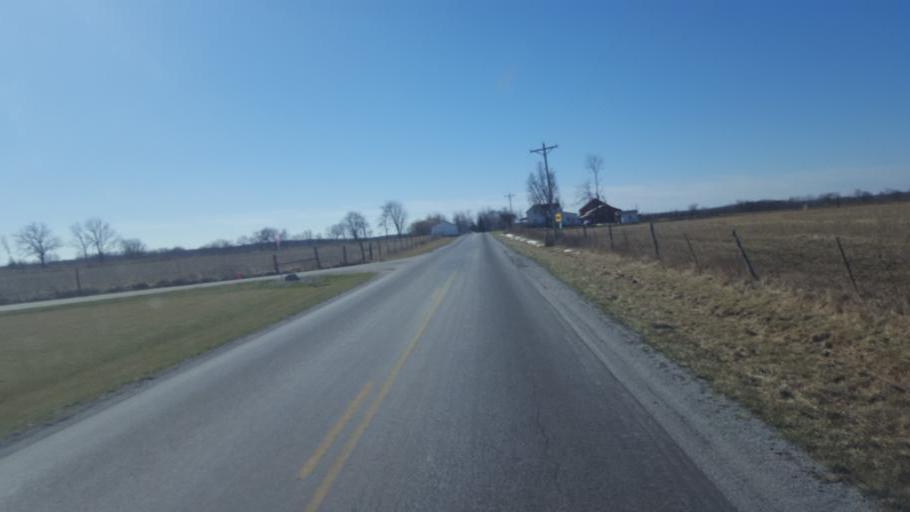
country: US
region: Ohio
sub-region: Hardin County
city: Kenton
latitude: 40.6288
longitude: -83.4896
